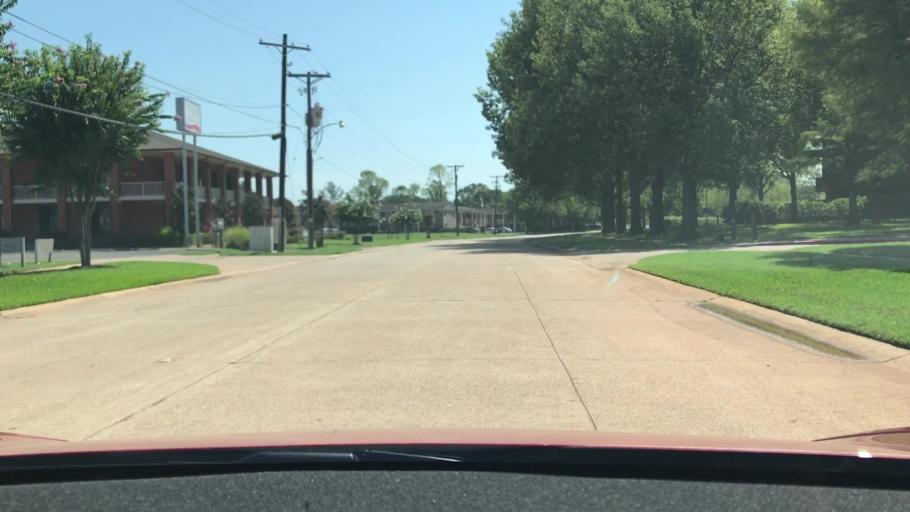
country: US
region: Louisiana
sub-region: Bossier Parish
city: Bossier City
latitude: 32.4488
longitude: -93.7211
